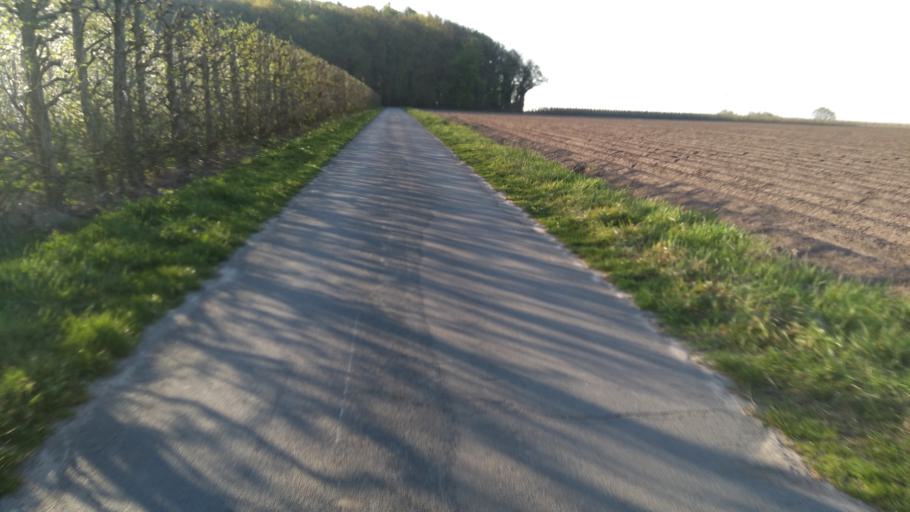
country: DE
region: Lower Saxony
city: Bliedersdorf
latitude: 53.4728
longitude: 9.5829
